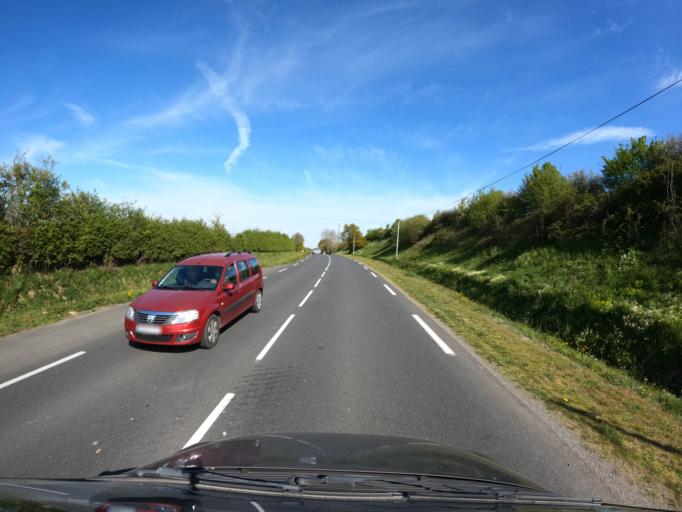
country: FR
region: Pays de la Loire
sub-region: Departement de Maine-et-Loire
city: Saint-Leger-sous-Cholet
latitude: 47.0693
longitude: -0.9141
